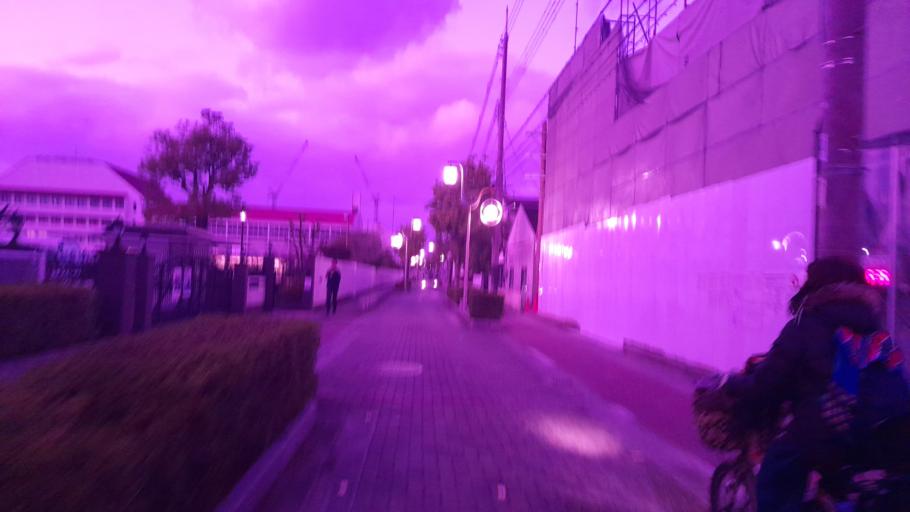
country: JP
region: Hyogo
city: Amagasaki
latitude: 34.7473
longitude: 135.4405
